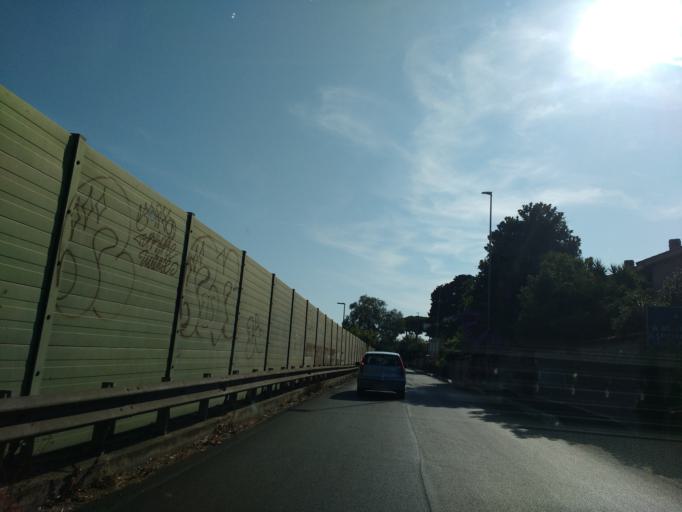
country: IT
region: Latium
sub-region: Citta metropolitana di Roma Capitale
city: Acilia-Castel Fusano-Ostia Antica
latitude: 41.7857
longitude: 12.3645
